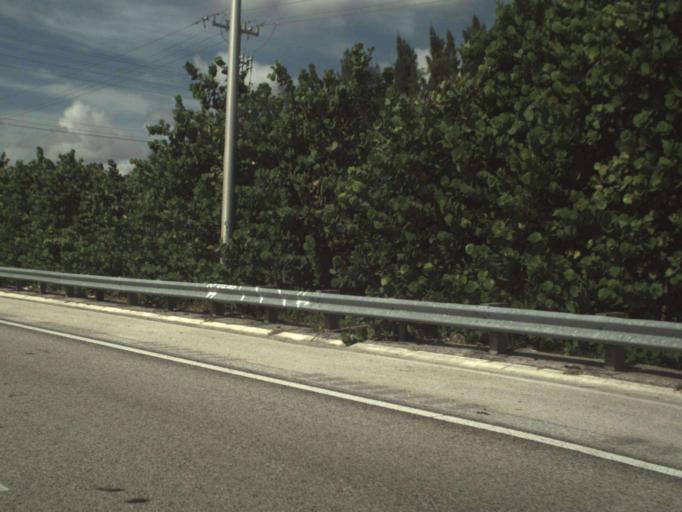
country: US
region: Florida
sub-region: Palm Beach County
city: Lake Clarke Shores
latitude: 26.6699
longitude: -80.0709
